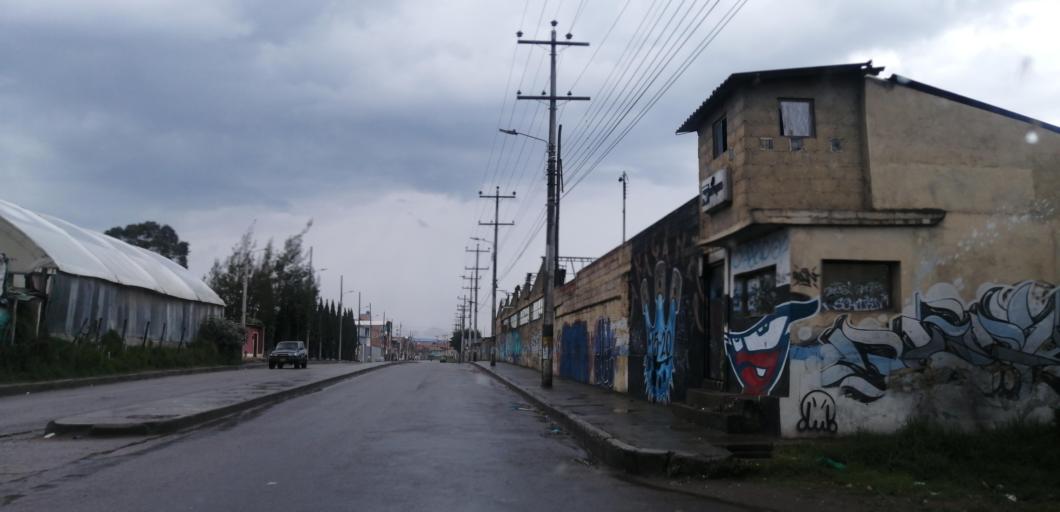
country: CO
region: Cundinamarca
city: Madrid
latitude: 4.7383
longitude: -74.2603
